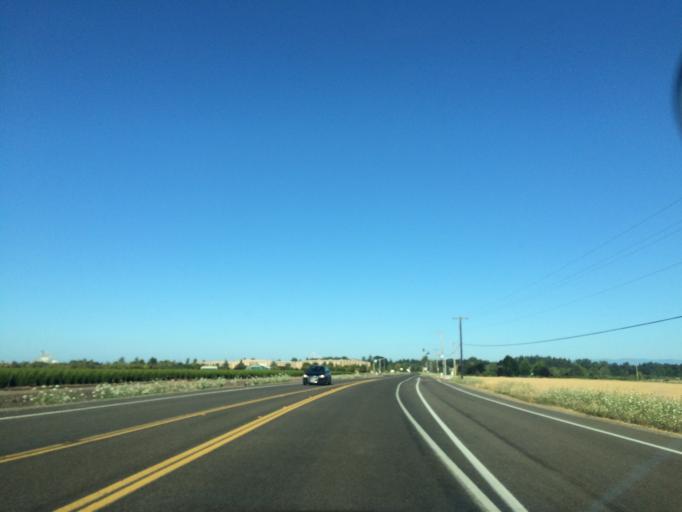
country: US
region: Oregon
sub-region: Marion County
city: Hubbard
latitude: 45.2306
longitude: -122.8387
